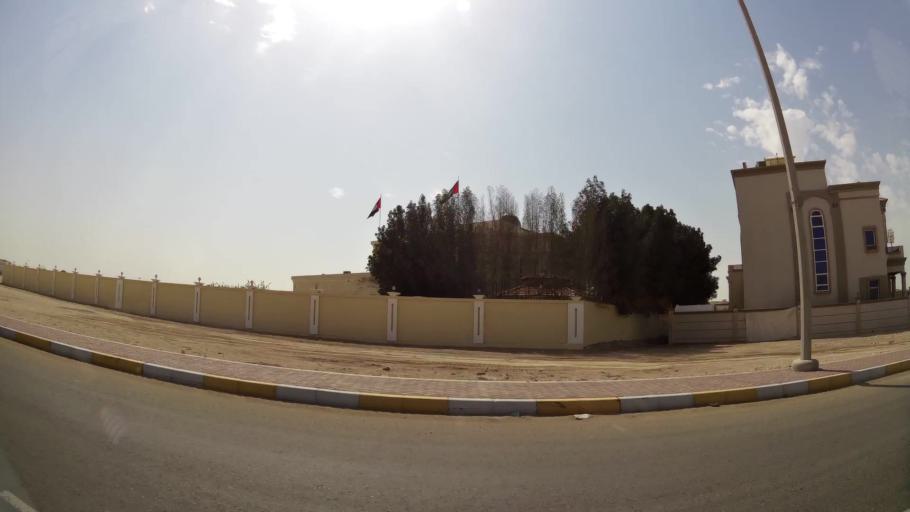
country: AE
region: Abu Dhabi
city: Abu Dhabi
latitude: 24.3358
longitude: 54.5660
